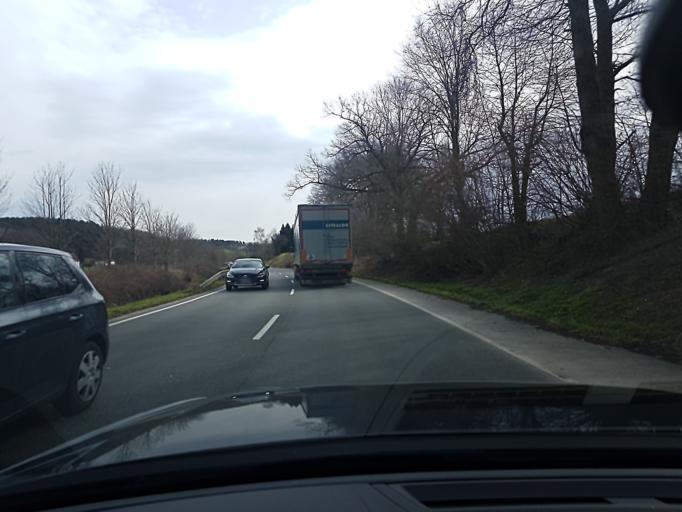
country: DE
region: North Rhine-Westphalia
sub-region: Regierungsbezirk Arnsberg
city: Holzwickede
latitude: 51.4393
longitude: 7.6694
